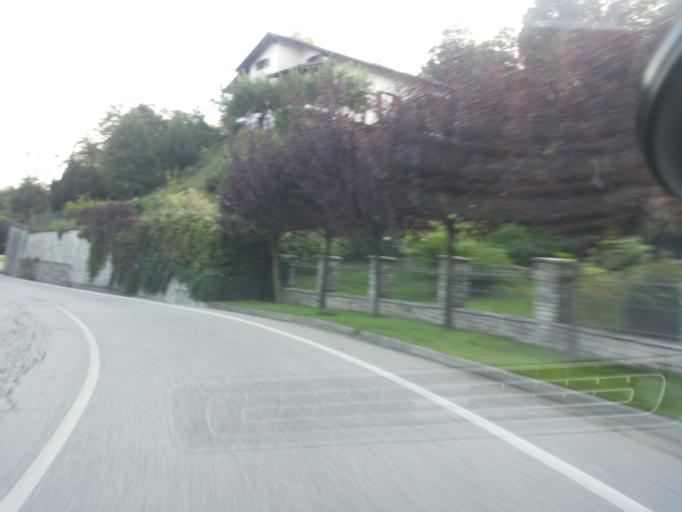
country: IT
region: Piedmont
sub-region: Provincia di Biella
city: Valle Mosso
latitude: 45.6390
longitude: 8.1524
